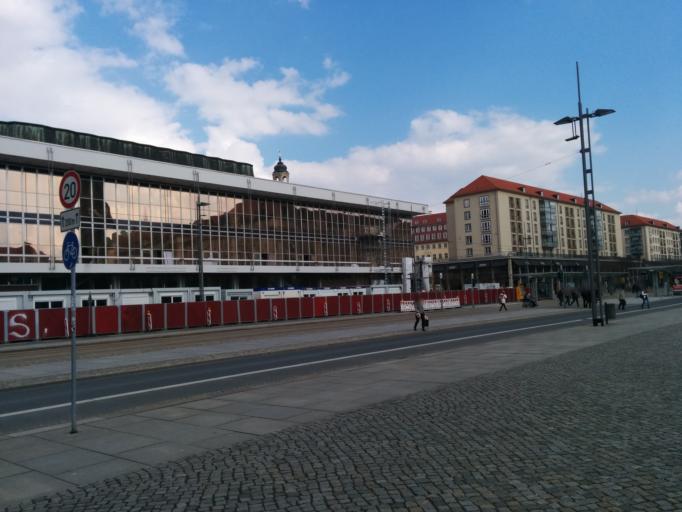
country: DE
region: Saxony
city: Dresden
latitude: 51.0501
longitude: 13.7374
